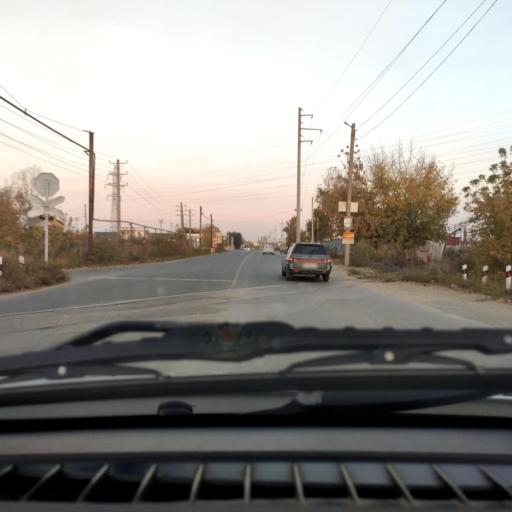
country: RU
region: Samara
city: Zhigulevsk
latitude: 53.5272
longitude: 49.4781
